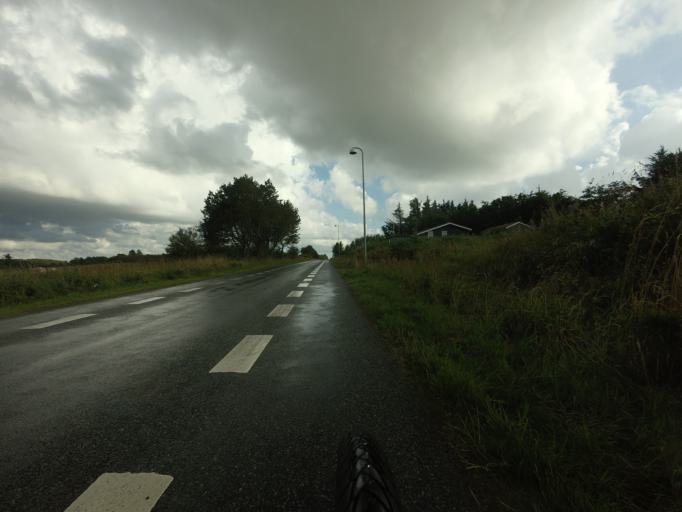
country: DK
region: North Denmark
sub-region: Hjorring Kommune
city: Hjorring
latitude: 57.4628
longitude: 9.7969
